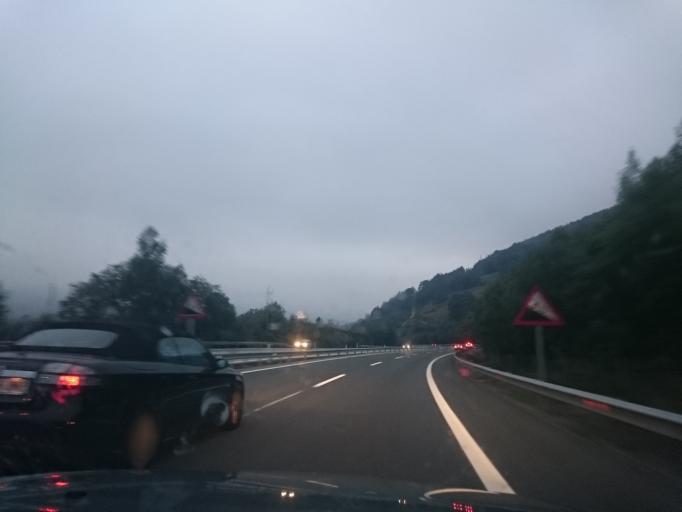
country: ES
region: Asturias
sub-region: Province of Asturias
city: Pola de Lena
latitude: 43.0433
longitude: -5.8195
